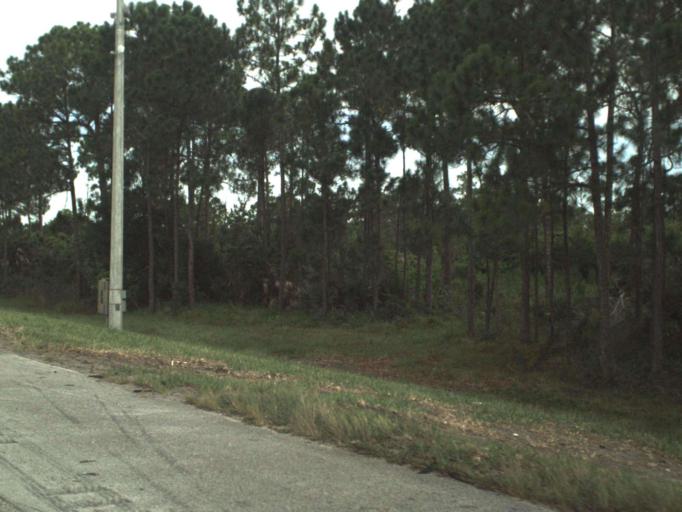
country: US
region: Florida
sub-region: Martin County
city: Palm City
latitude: 27.1271
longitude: -80.2886
